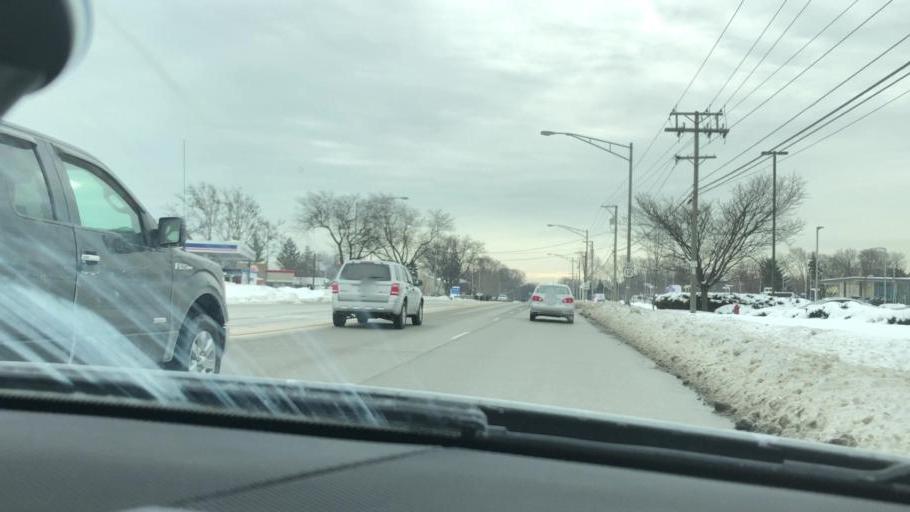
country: US
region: Illinois
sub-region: Cook County
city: Mount Prospect
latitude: 42.0660
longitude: -87.9205
